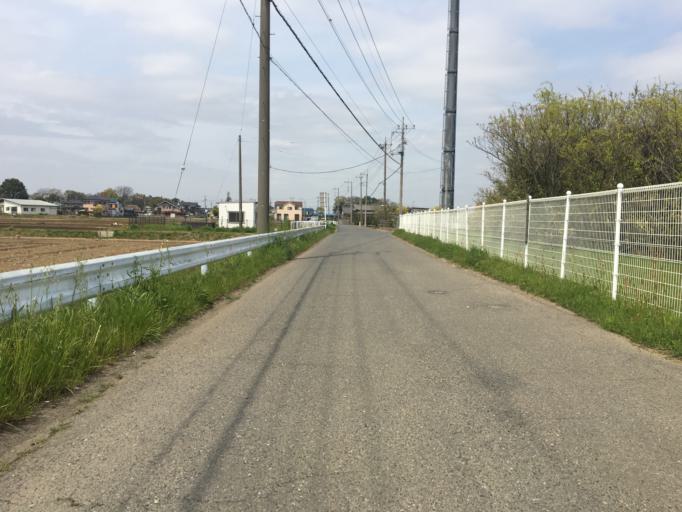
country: JP
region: Saitama
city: Kamifukuoka
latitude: 35.8867
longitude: 139.5485
